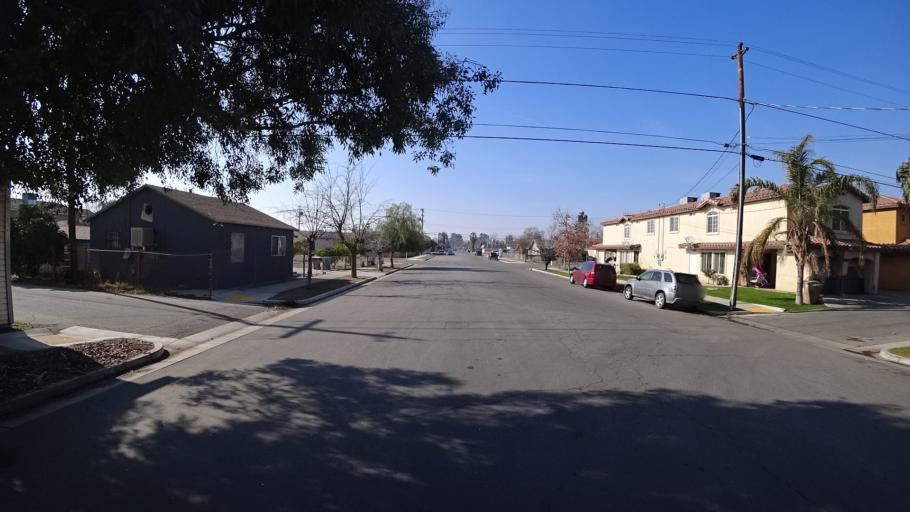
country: US
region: California
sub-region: Kern County
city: Bakersfield
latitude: 35.3637
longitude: -119.0170
